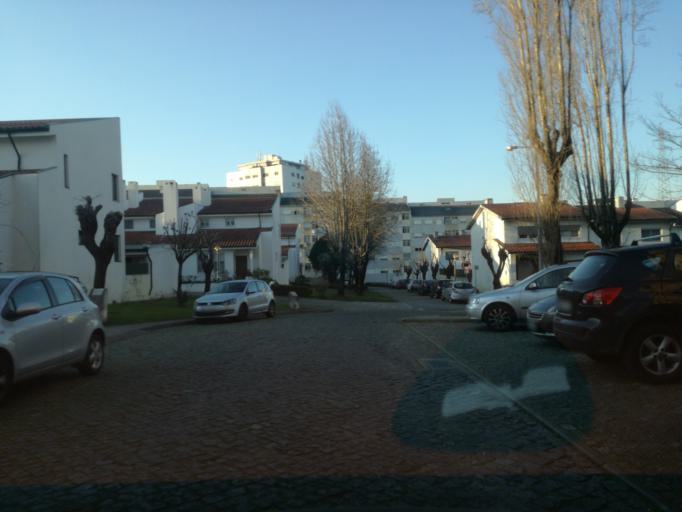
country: PT
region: Porto
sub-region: Maia
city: Leca do Bailio
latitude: 41.2225
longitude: -8.6074
